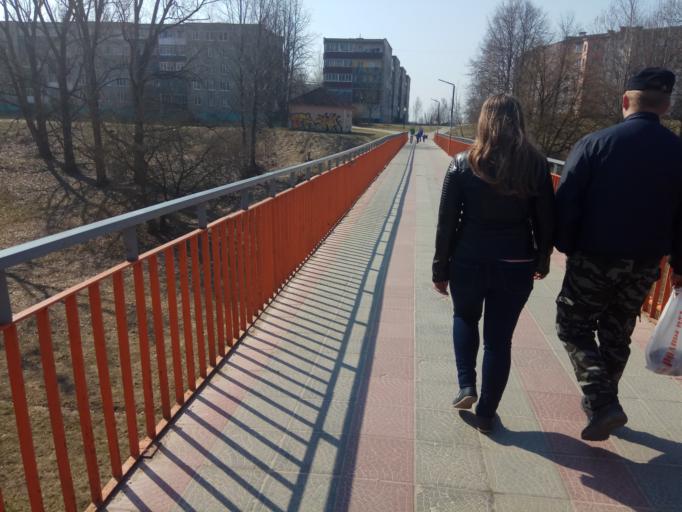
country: BY
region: Minsk
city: Valozhyn
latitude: 54.0879
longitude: 26.5215
